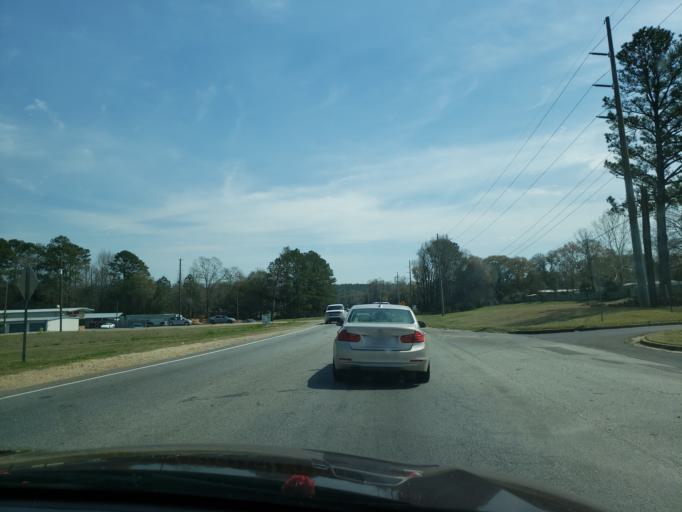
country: US
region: Alabama
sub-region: Autauga County
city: Prattville
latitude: 32.4375
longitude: -86.4712
